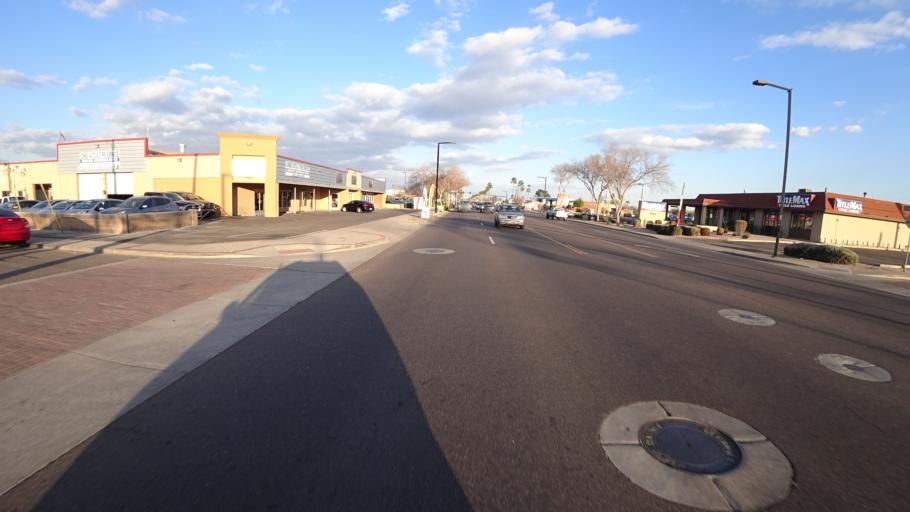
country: US
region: Arizona
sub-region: Maricopa County
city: Glendale
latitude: 33.5385
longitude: -112.1706
